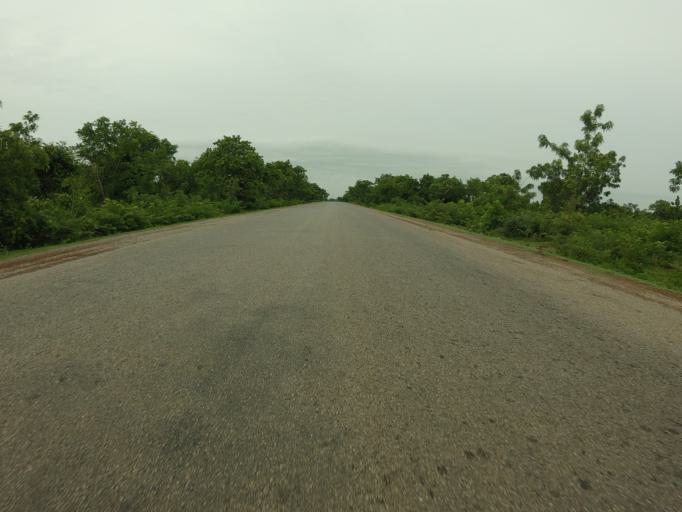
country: GH
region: Northern
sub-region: Yendi
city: Yendi
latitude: 9.5206
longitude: -0.0290
